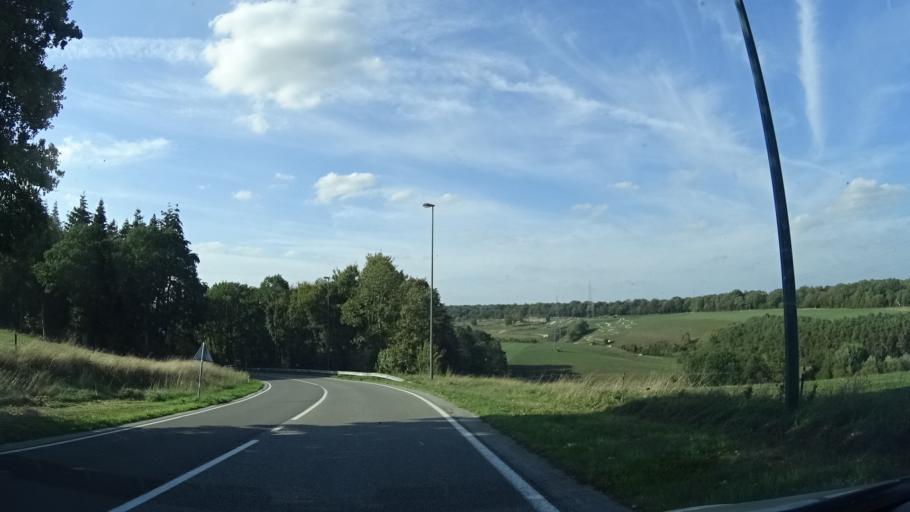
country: BE
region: Wallonia
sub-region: Province de Namur
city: Cerfontaine
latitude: 50.1935
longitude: 4.3818
